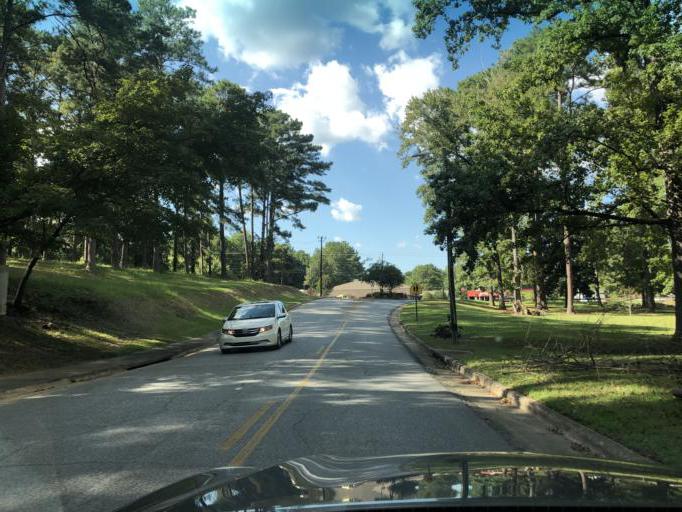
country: US
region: Georgia
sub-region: Muscogee County
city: Columbus
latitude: 32.5385
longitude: -84.9338
